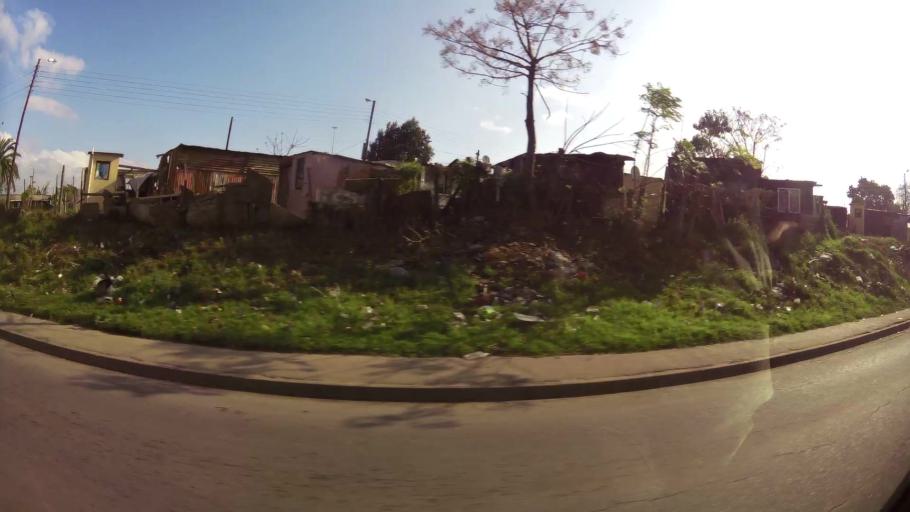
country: ZA
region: Eastern Cape
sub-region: Nelson Mandela Bay Metropolitan Municipality
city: Uitenhage
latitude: -33.7554
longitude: 25.3879
